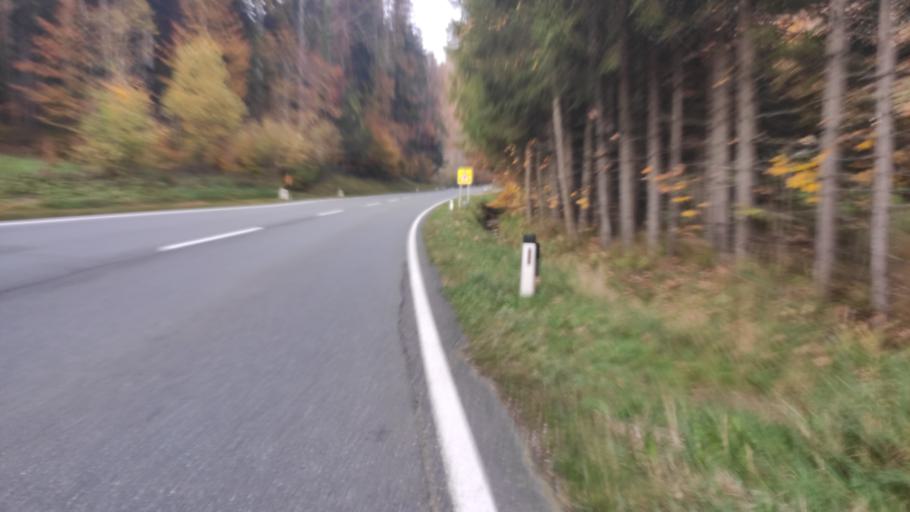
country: AT
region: Salzburg
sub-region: Politischer Bezirk Salzburg-Umgebung
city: Hof bei Salzburg
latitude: 47.8051
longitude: 13.1962
